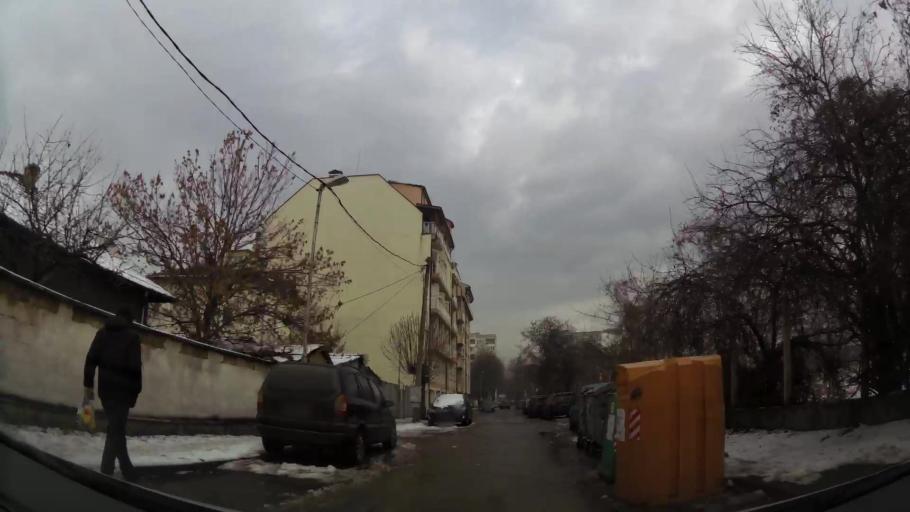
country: BG
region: Sofia-Capital
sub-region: Stolichna Obshtina
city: Sofia
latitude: 42.6915
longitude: 23.2858
